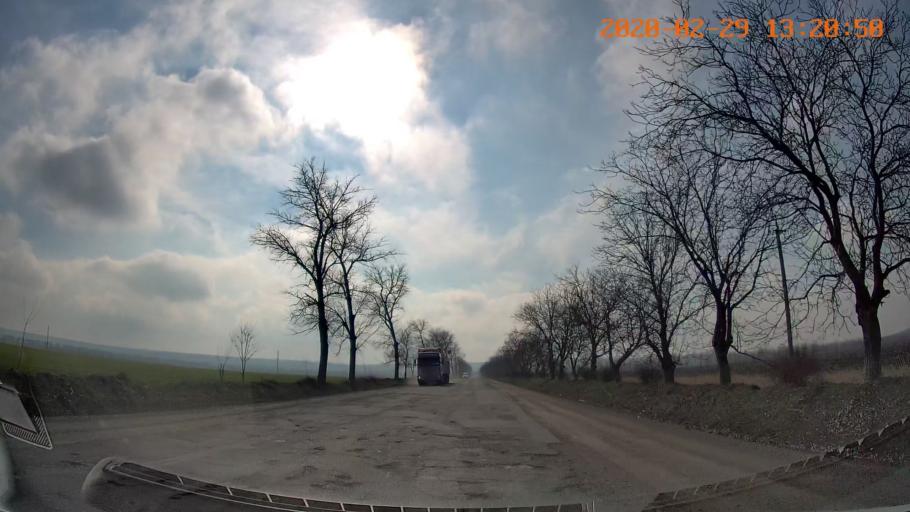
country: MD
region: Telenesti
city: Camenca
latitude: 47.9754
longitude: 28.6380
